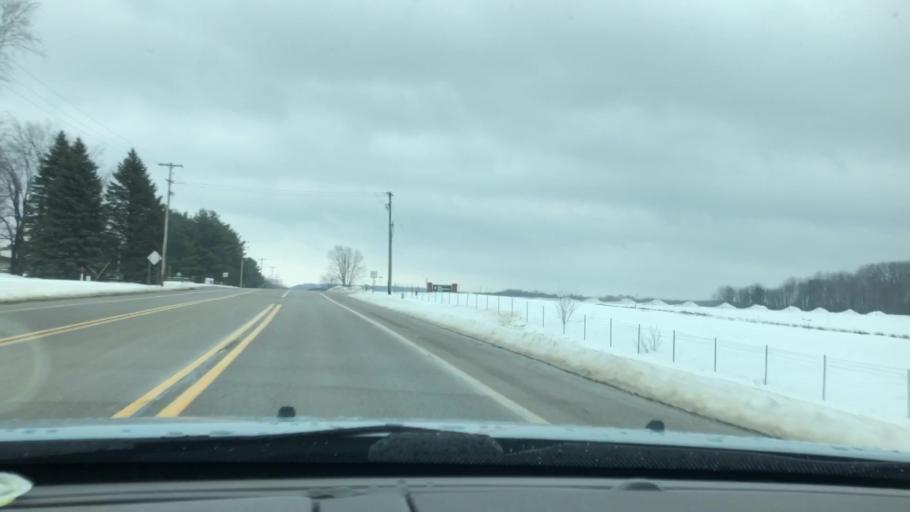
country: US
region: Michigan
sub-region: Charlevoix County
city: East Jordan
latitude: 45.1325
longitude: -85.1151
